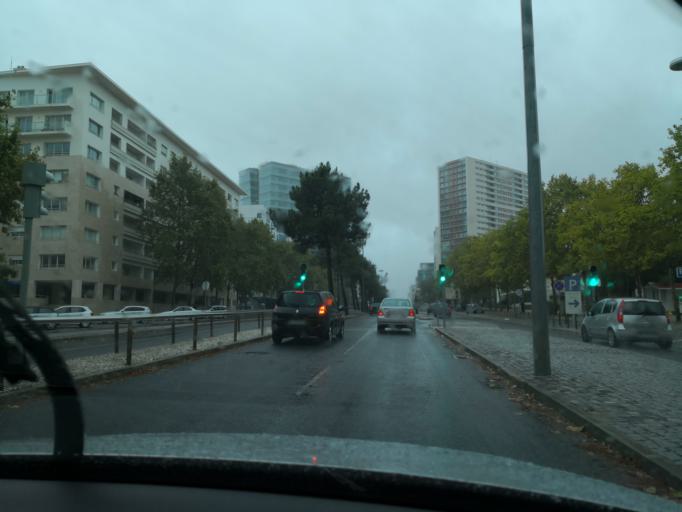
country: PT
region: Lisbon
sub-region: Loures
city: Moscavide
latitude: 38.7772
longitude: -9.0971
